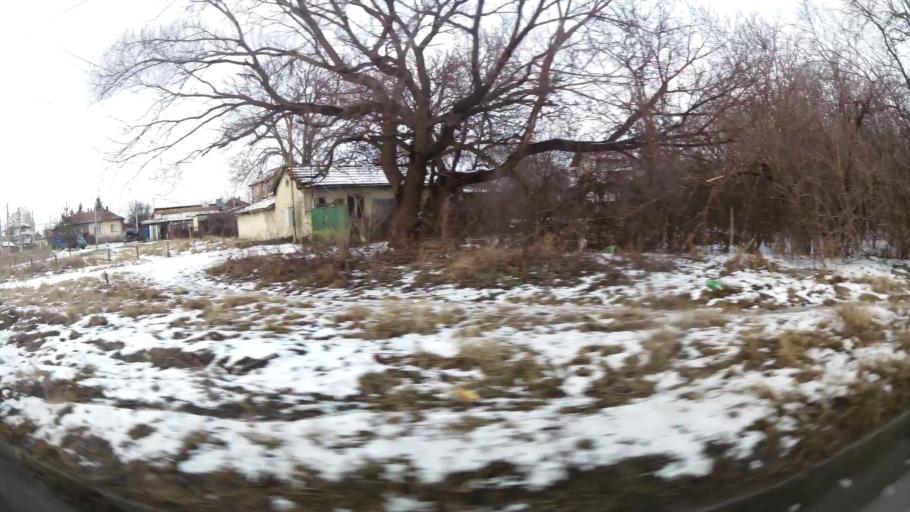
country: BG
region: Sofia-Capital
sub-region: Stolichna Obshtina
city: Sofia
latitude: 42.7238
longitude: 23.3472
